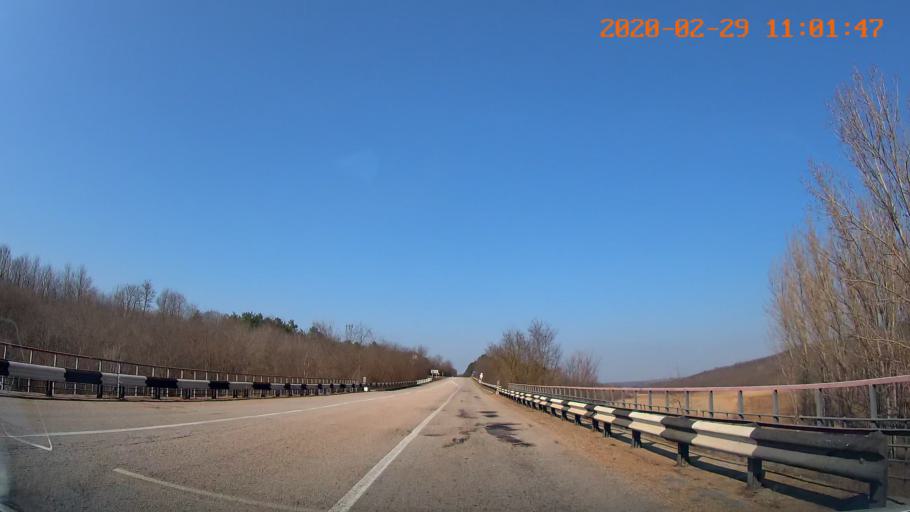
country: MD
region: Telenesti
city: Grigoriopol
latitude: 47.1671
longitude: 29.2511
